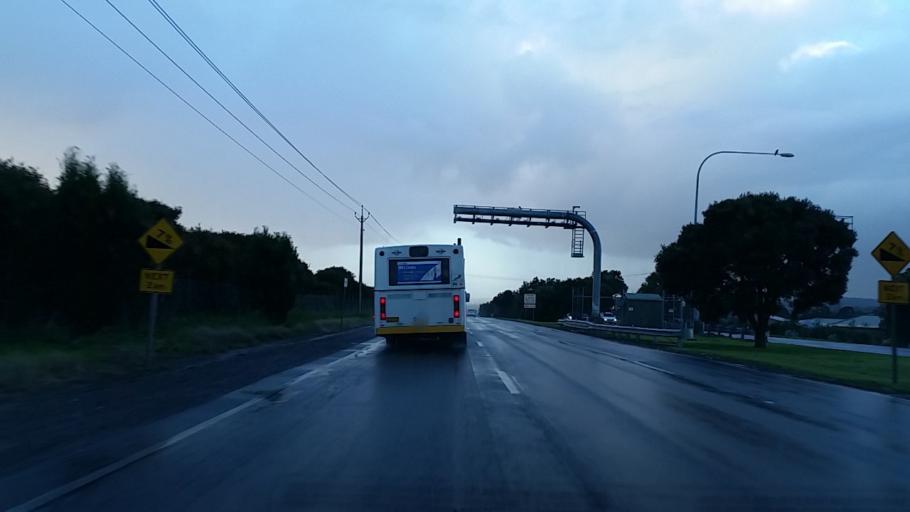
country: AU
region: South Australia
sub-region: Onkaparinga
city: Bedford Park
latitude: -35.0488
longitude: 138.5595
